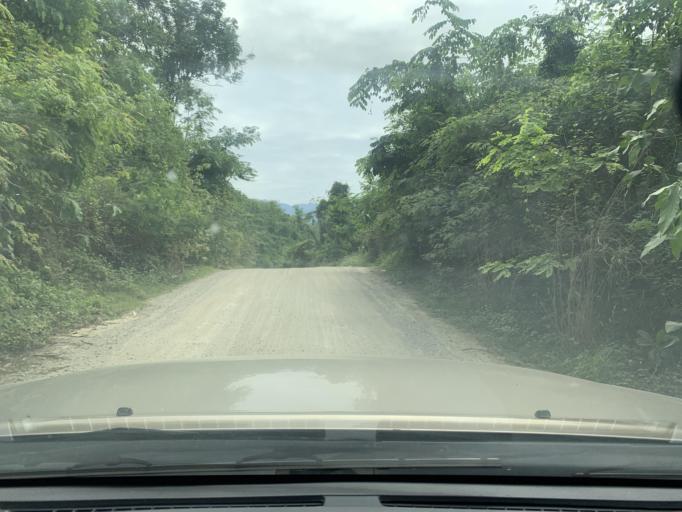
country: LA
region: Louangphabang
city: Louangphabang
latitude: 19.8862
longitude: 102.1863
